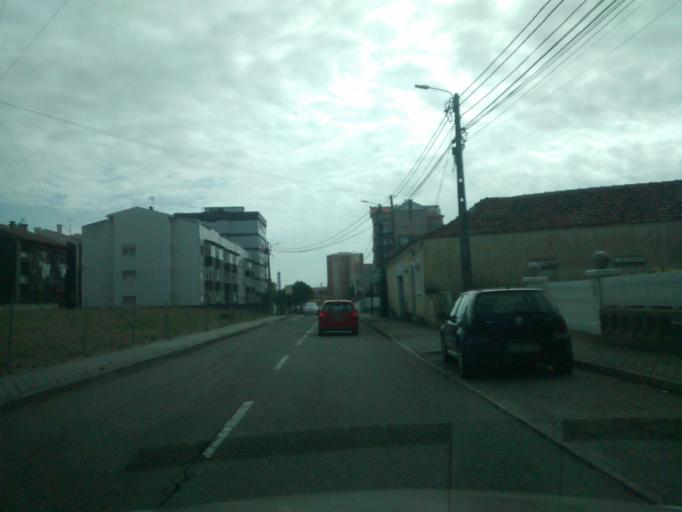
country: PT
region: Aveiro
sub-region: Aveiro
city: Aveiro
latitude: 40.6553
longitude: -8.6218
